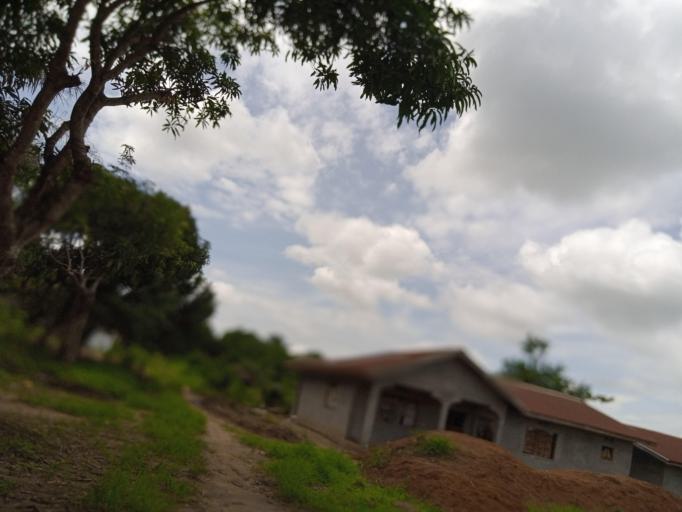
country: SL
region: Northern Province
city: Masoyila
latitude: 8.5921
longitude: -13.1817
